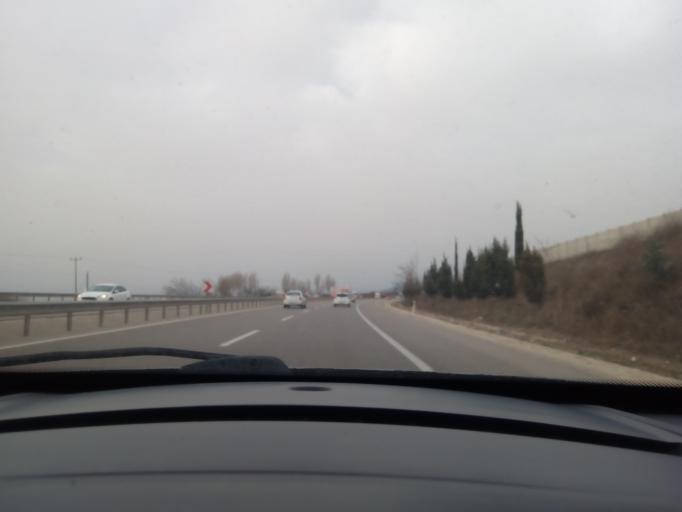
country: TR
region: Bursa
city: Mahmudiye
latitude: 40.2085
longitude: 28.5960
